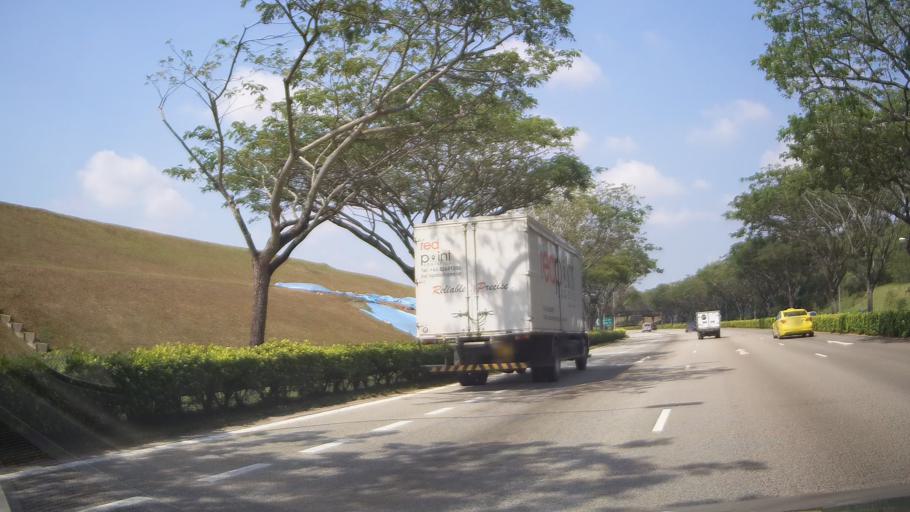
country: MY
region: Johor
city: Kampung Pasir Gudang Baru
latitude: 1.3779
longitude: 103.9125
